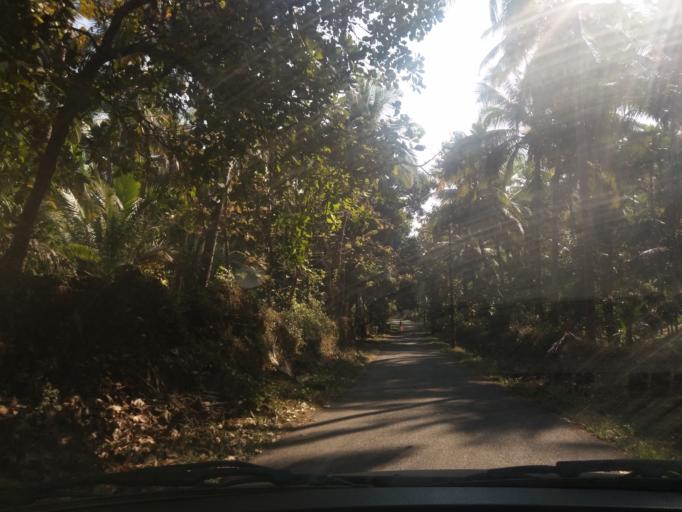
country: IN
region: Goa
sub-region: South Goa
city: Quepem
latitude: 15.1597
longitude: 74.0958
